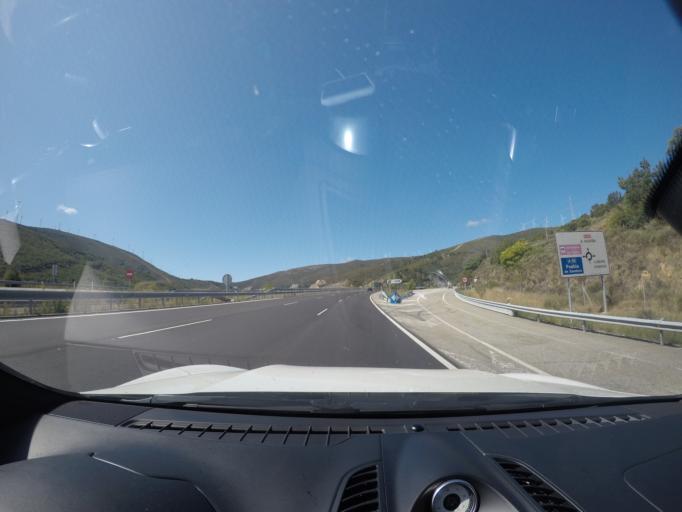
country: ES
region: Castille and Leon
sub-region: Provincia de Zamora
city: Lubian
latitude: 42.0349
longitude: -6.9327
